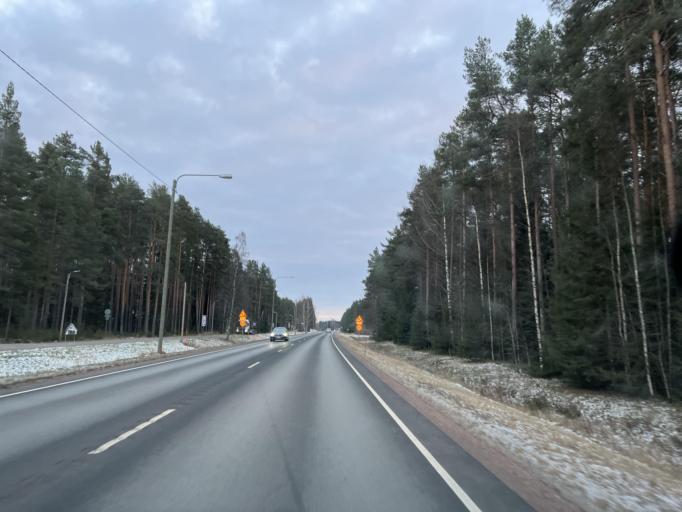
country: FI
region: Northern Ostrobothnia
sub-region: Oulu
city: Muhos
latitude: 64.8792
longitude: 25.8516
